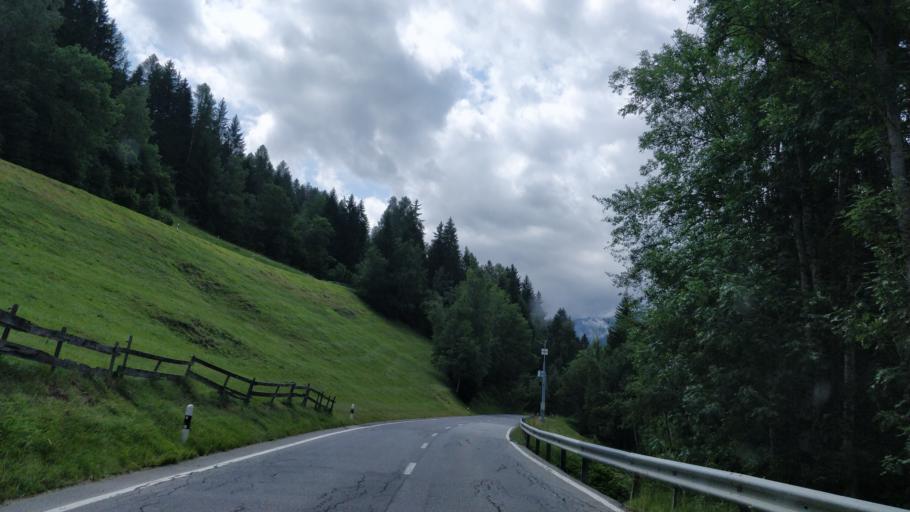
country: CH
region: Grisons
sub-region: Surselva District
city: Ilanz
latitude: 46.7096
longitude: 9.1939
